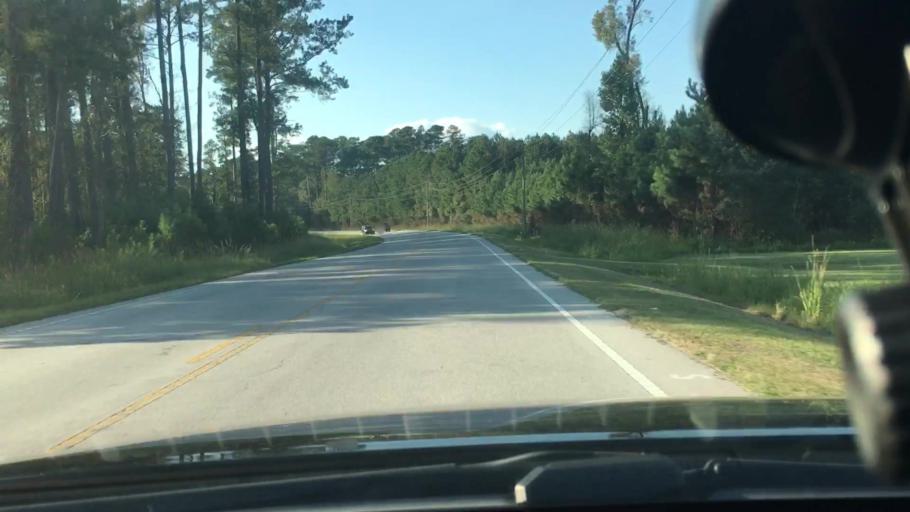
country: US
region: North Carolina
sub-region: Pitt County
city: Windsor
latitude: 35.4681
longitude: -77.2785
